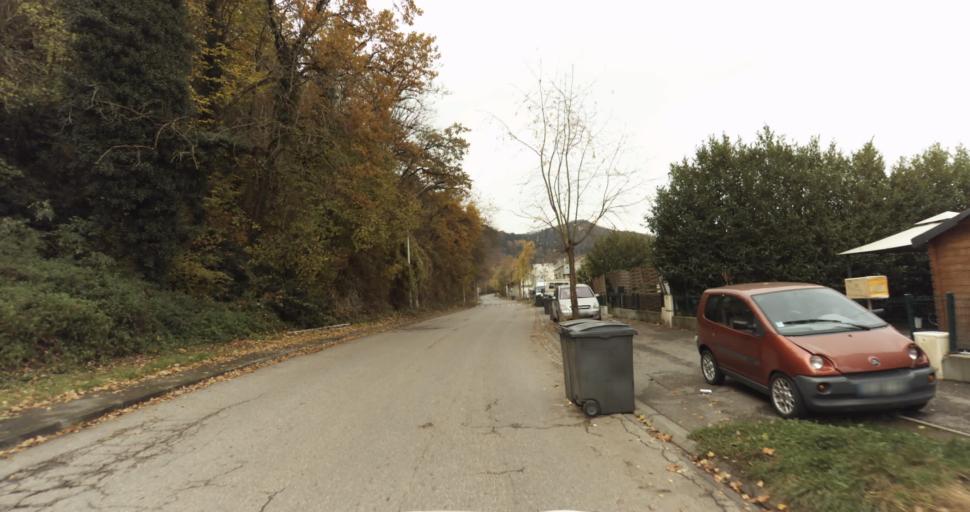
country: FR
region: Rhone-Alpes
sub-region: Departement de la Haute-Savoie
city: Annecy
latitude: 45.8854
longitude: 6.1212
